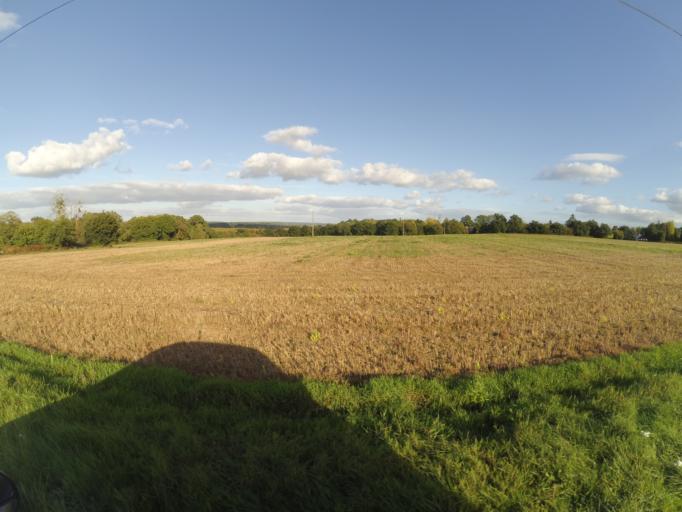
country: FR
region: Brittany
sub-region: Departement du Morbihan
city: Saint-Vincent-sur-Oust
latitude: 47.7183
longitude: -2.1788
